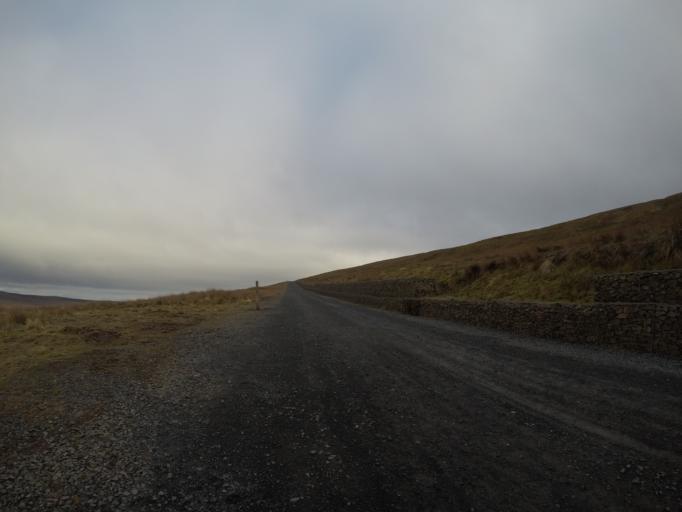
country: GB
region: Scotland
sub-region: North Ayrshire
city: Fairlie
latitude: 55.7639
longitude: -4.7977
